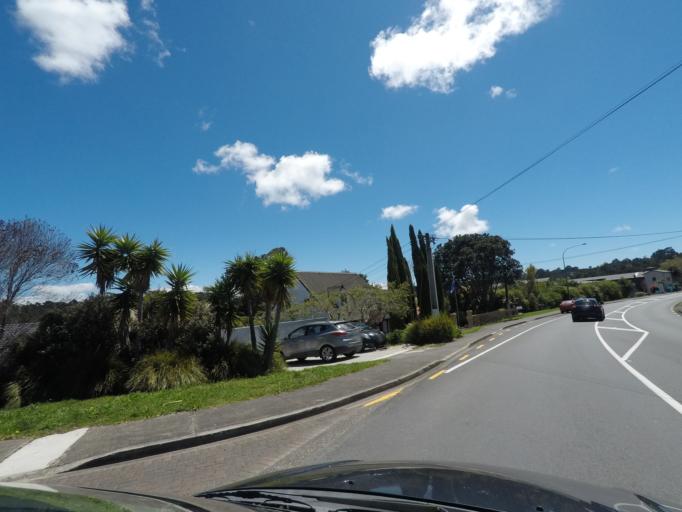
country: NZ
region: Auckland
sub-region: Auckland
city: Rothesay Bay
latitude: -36.7255
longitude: 174.6882
